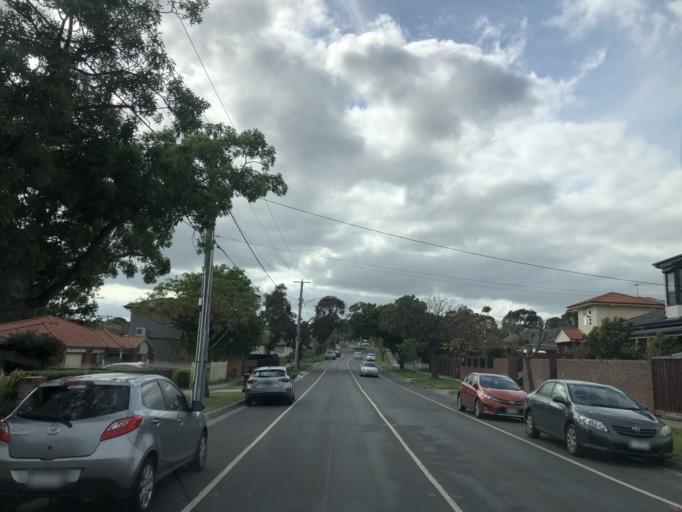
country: AU
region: Victoria
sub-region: Monash
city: Chadstone
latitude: -37.8756
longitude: 145.0952
